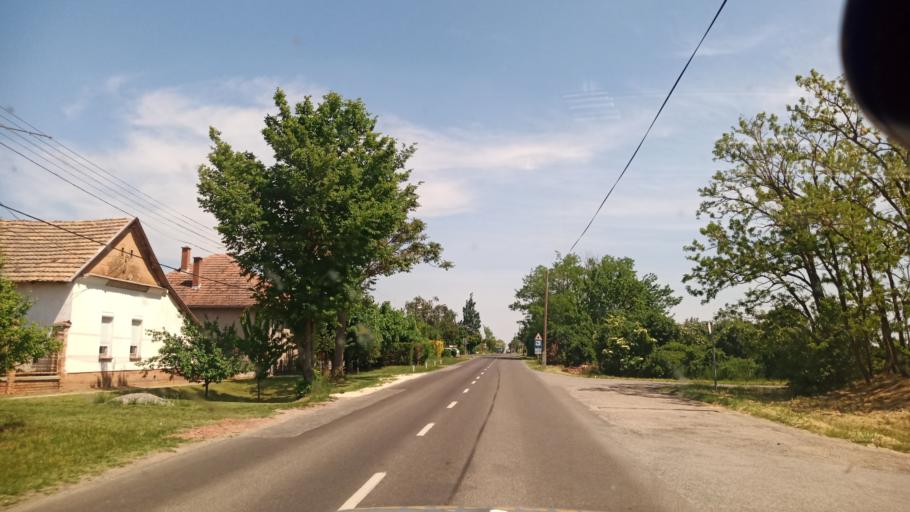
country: HU
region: Bekes
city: Oroshaza
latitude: 46.5662
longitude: 20.5928
